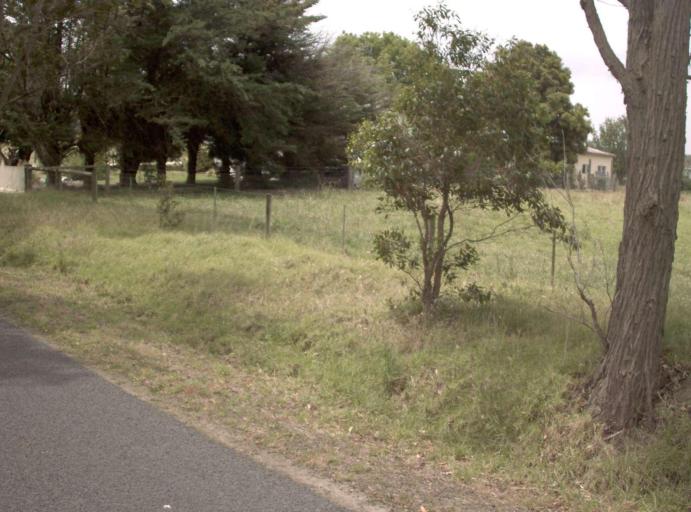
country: AU
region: Victoria
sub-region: Latrobe
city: Traralgon
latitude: -38.4817
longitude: 146.6816
